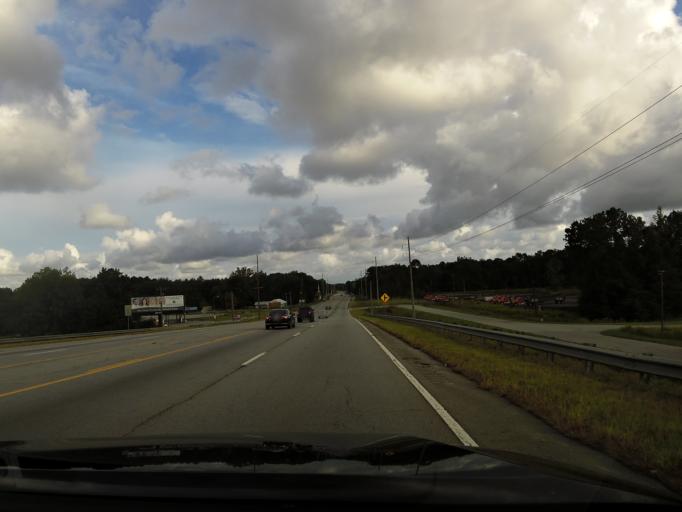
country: US
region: Georgia
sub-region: Liberty County
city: Hinesville
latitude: 31.8268
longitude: -81.5254
